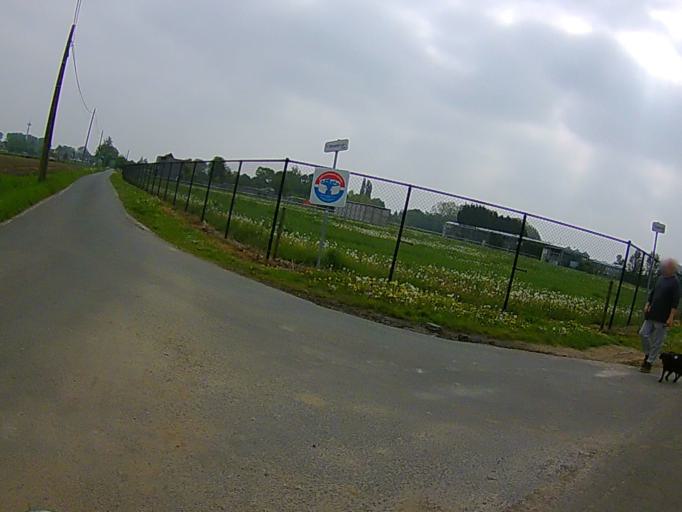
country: BE
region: Flanders
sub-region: Provincie Antwerpen
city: Wommelgem
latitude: 51.1900
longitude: 4.5301
